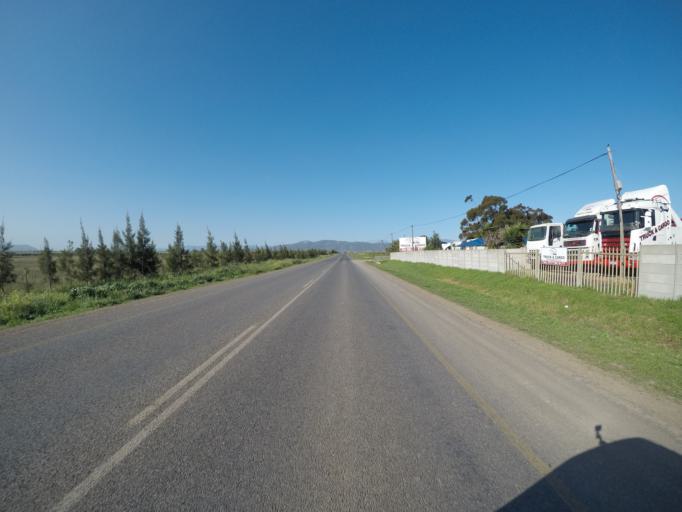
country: ZA
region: Western Cape
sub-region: City of Cape Town
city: Kraaifontein
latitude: -33.7661
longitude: 18.7892
